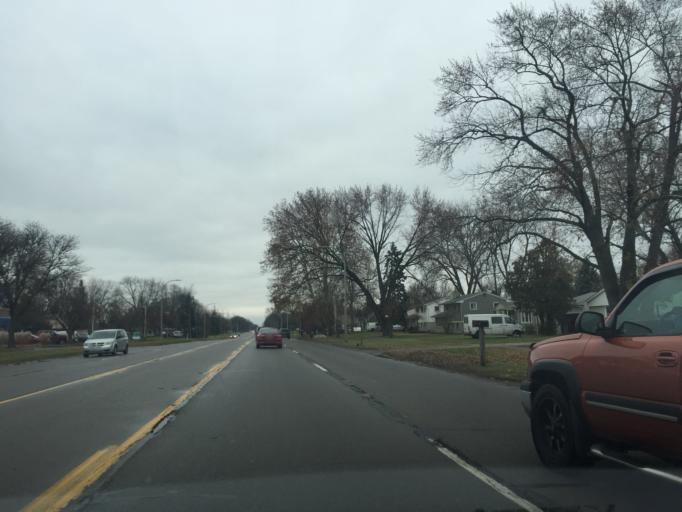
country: US
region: Michigan
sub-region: Wayne County
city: Redford
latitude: 42.4244
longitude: -83.3358
